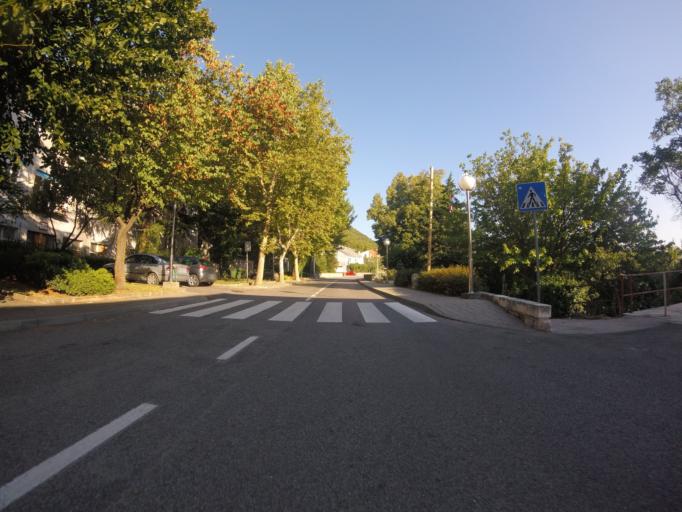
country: HR
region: Primorsko-Goranska
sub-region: Grad Crikvenica
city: Crikvenica
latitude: 45.2021
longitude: 14.7189
